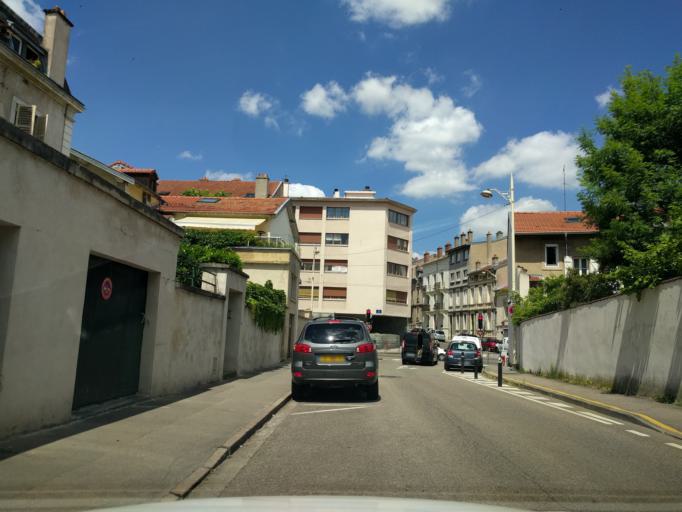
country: FR
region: Lorraine
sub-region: Departement de Meurthe-et-Moselle
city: Laxou
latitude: 48.6860
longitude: 6.1639
